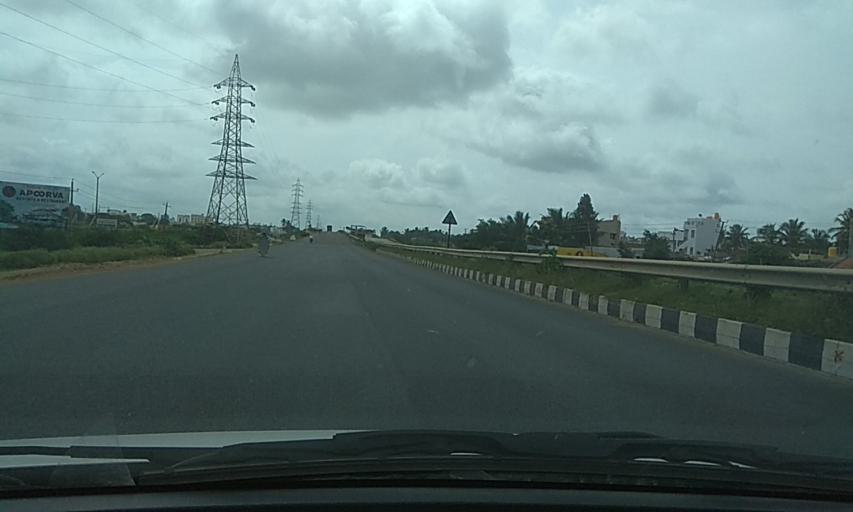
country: IN
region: Karnataka
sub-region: Davanagere
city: Harihar
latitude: 14.4432
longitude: 75.8951
